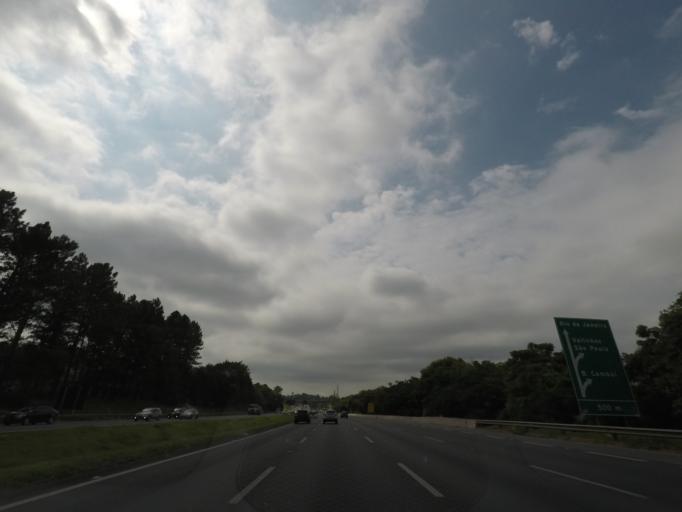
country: BR
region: Sao Paulo
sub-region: Campinas
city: Campinas
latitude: -22.8898
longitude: -47.0110
